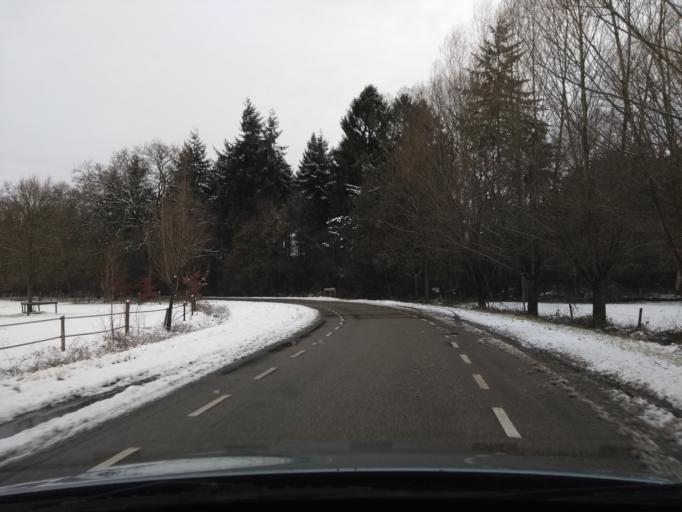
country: NL
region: Overijssel
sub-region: Gemeente Haaksbergen
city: Haaksbergen
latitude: 52.1430
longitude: 6.7478
